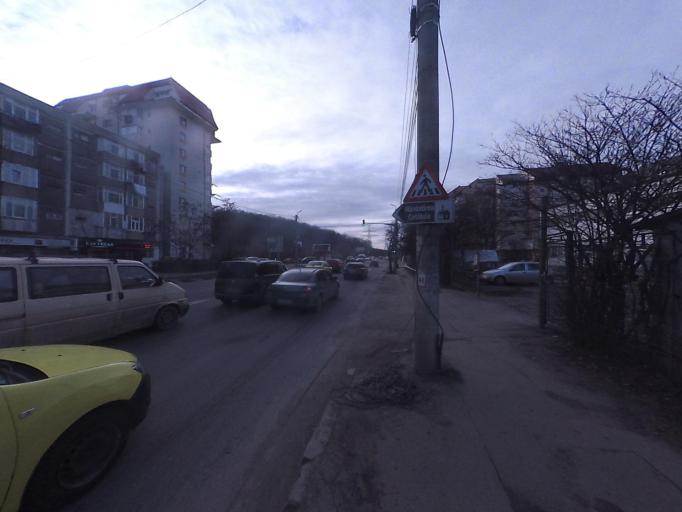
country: RO
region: Iasi
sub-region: Municipiul Iasi
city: Iasi
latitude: 47.1357
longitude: 27.5884
